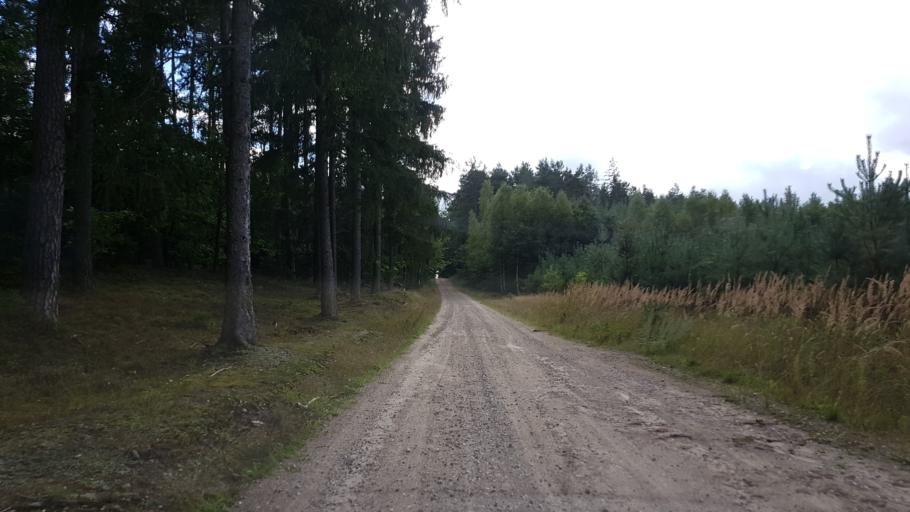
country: PL
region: West Pomeranian Voivodeship
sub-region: Powiat bialogardzki
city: Tychowo
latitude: 54.0077
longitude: 16.3023
